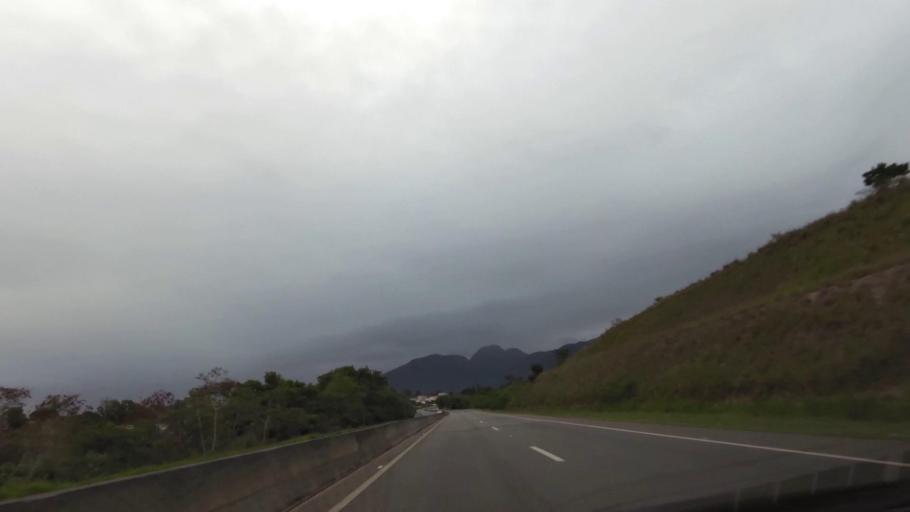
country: BR
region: Espirito Santo
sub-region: Guarapari
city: Guarapari
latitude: -20.6147
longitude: -40.4484
